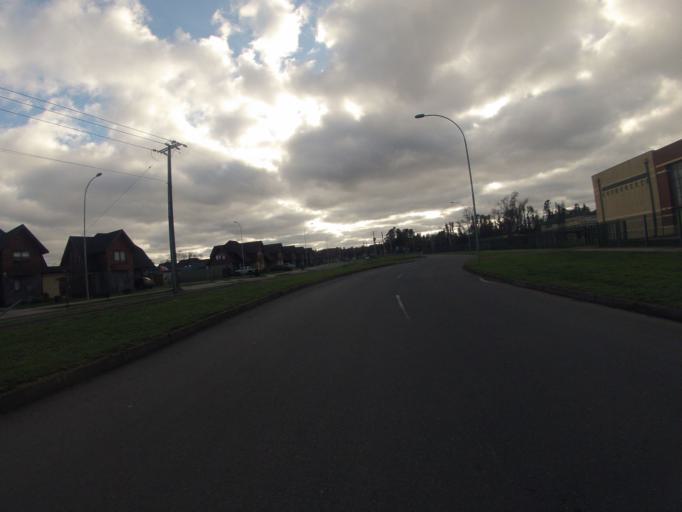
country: CL
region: Araucania
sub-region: Provincia de Cautin
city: Temuco
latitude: -38.7411
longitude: -72.6501
